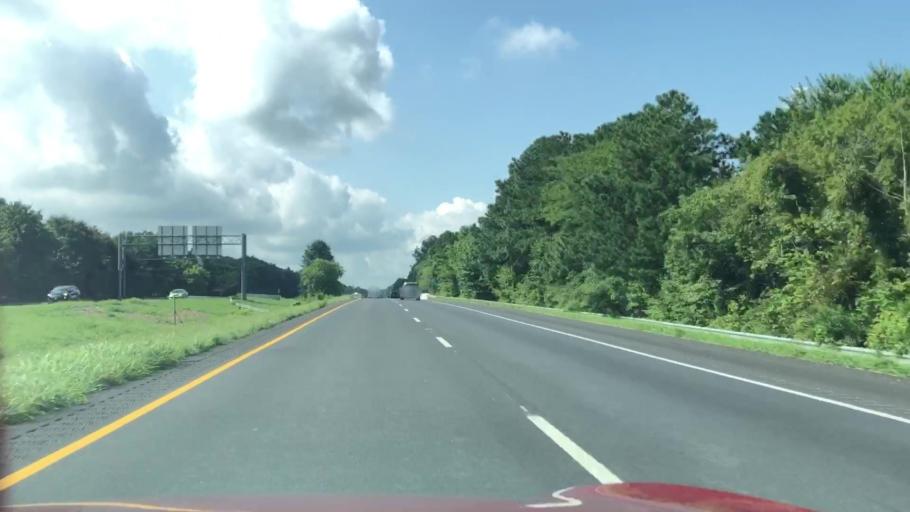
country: US
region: Maryland
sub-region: Wicomico County
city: Salisbury
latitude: 38.3588
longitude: -75.5396
